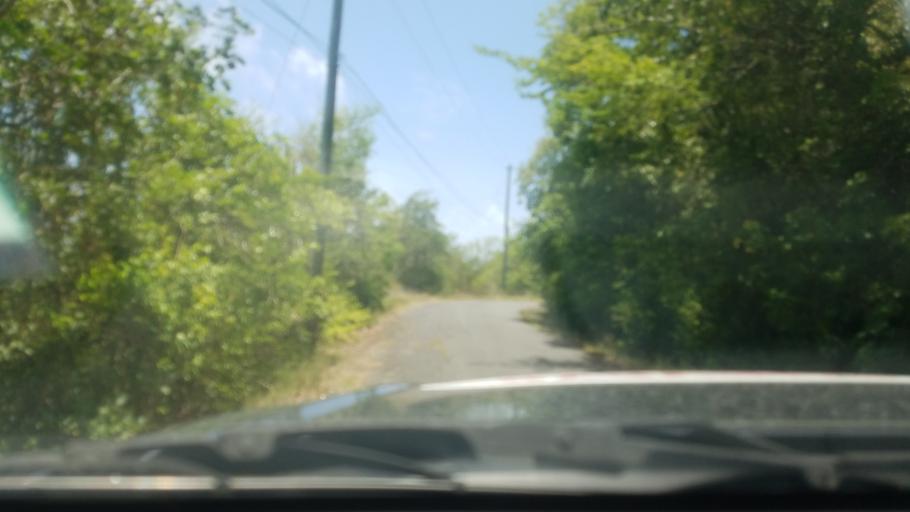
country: LC
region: Vieux-Fort
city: Vieux Fort
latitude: 13.7127
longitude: -60.9444
